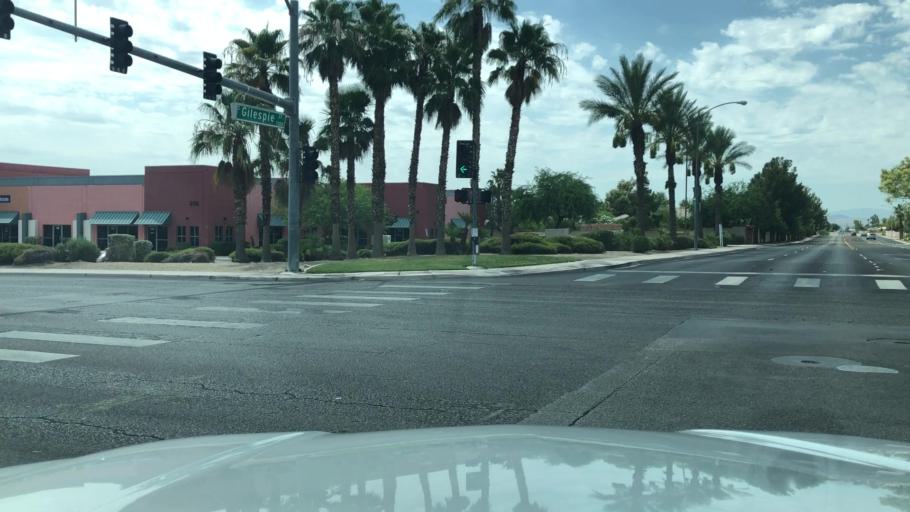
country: US
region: Nevada
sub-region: Clark County
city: Paradise
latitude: 36.0570
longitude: -115.1633
